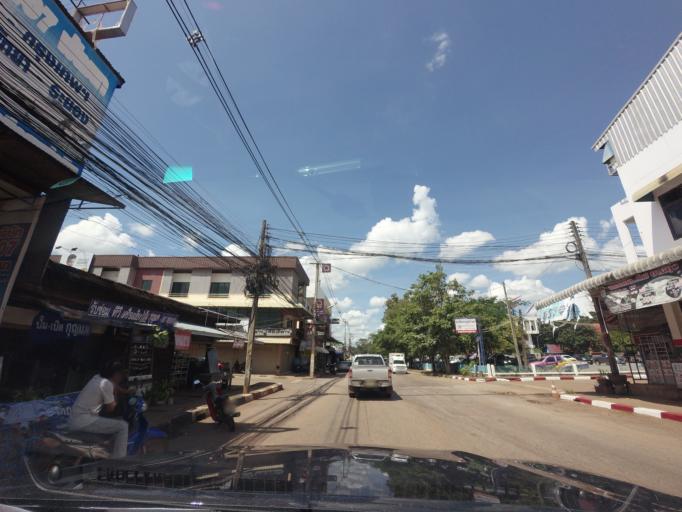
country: TH
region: Changwat Udon Thani
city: Ban Dung
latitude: 17.7006
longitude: 103.2577
